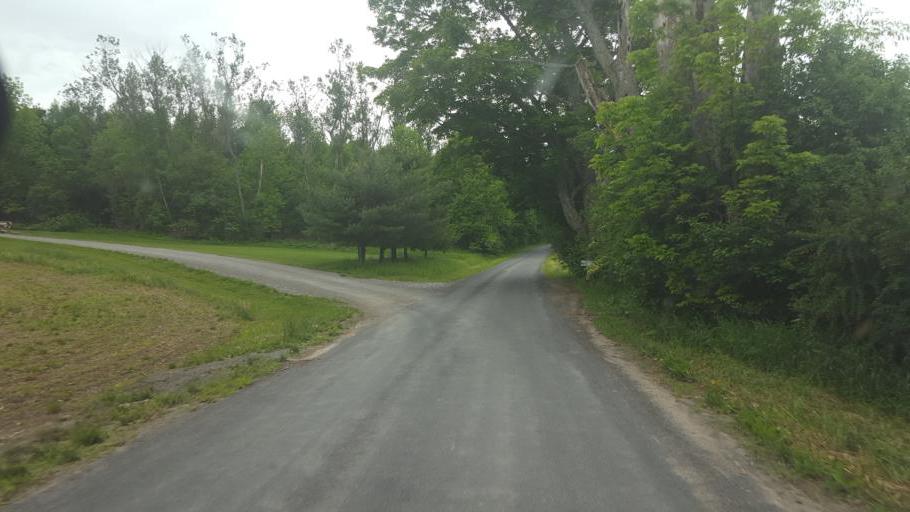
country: US
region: New York
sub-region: Oneida County
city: Chadwicks
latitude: 42.8688
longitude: -75.1757
